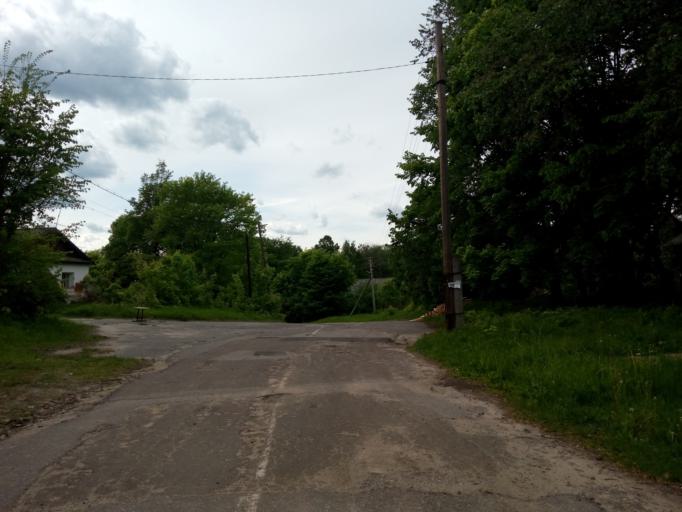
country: RU
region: Nizjnij Novgorod
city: Voskresenskoye
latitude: 56.7797
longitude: 45.5350
